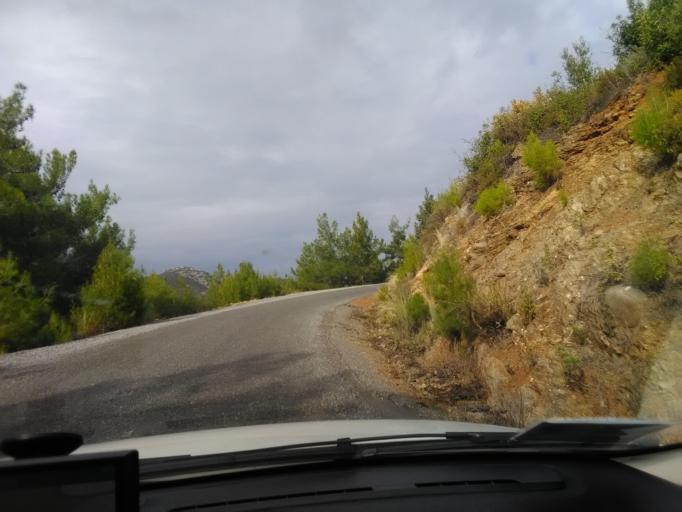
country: TR
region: Antalya
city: Gazipasa
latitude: 36.2488
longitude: 32.4215
